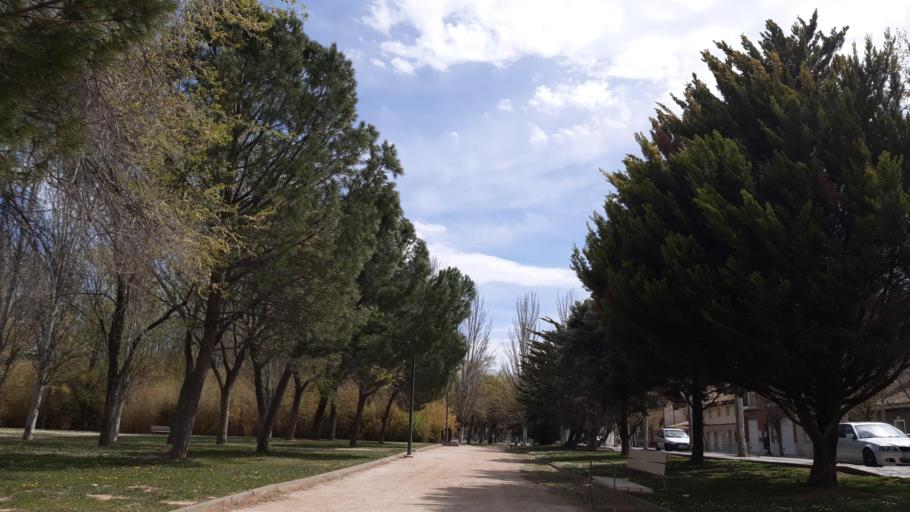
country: ES
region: Aragon
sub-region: Provincia de Zaragoza
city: Utebo
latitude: 41.7129
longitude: -1.0048
